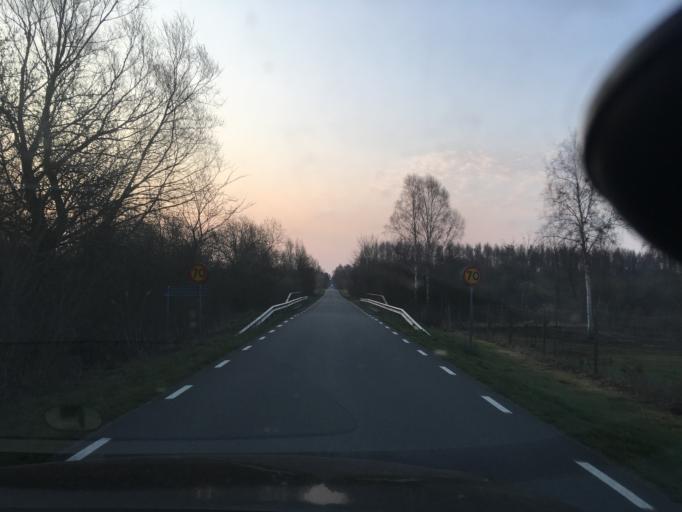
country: SE
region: Skane
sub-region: Simrishamns Kommun
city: Simrishamn
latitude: 55.3995
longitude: 14.1669
